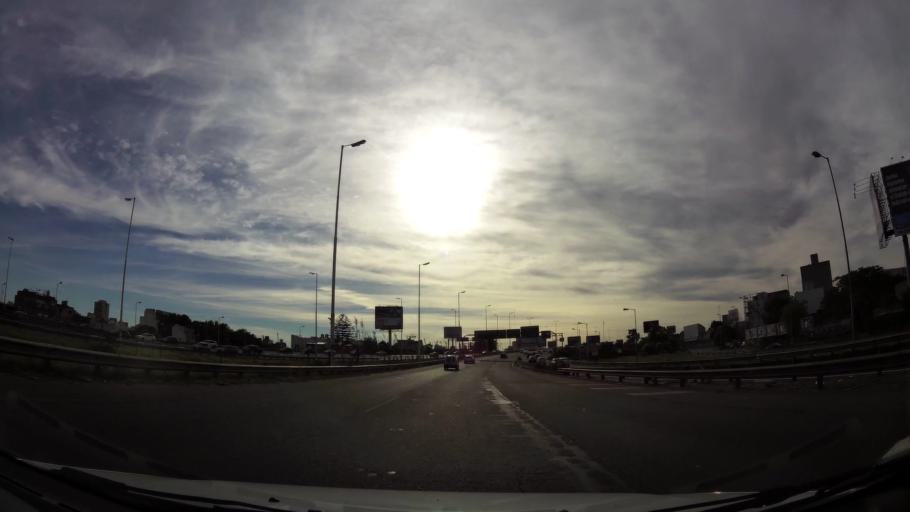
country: AR
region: Buenos Aires
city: Caseros
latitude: -34.6347
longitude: -58.5354
